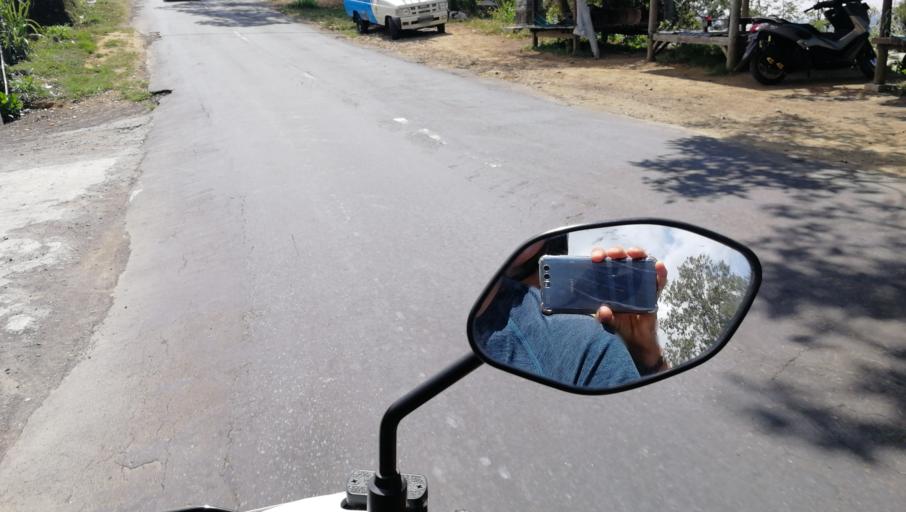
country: ID
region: Bali
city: Munduk
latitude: -8.2369
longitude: 115.1367
